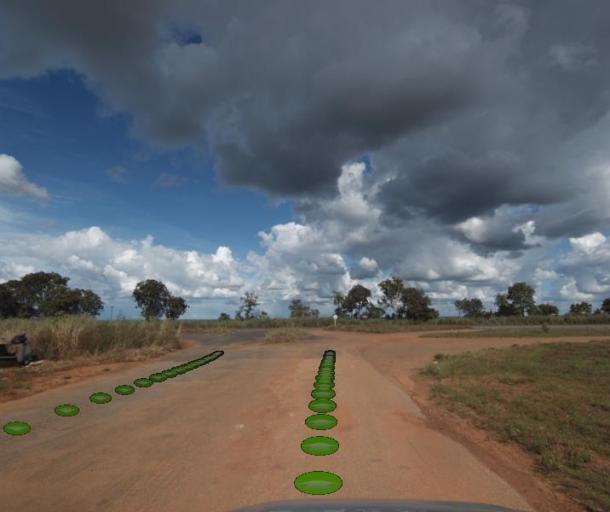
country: BR
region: Goias
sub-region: Porangatu
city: Porangatu
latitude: -13.1023
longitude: -49.1995
